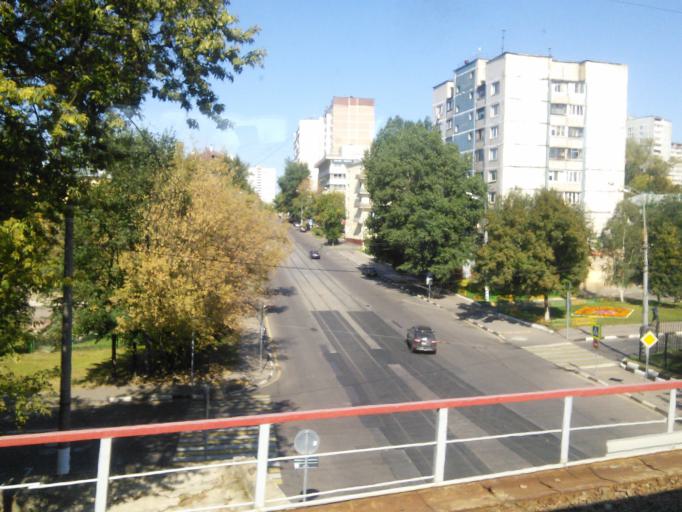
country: RU
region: Moscow
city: Taganskiy
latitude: 55.7496
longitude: 37.6761
